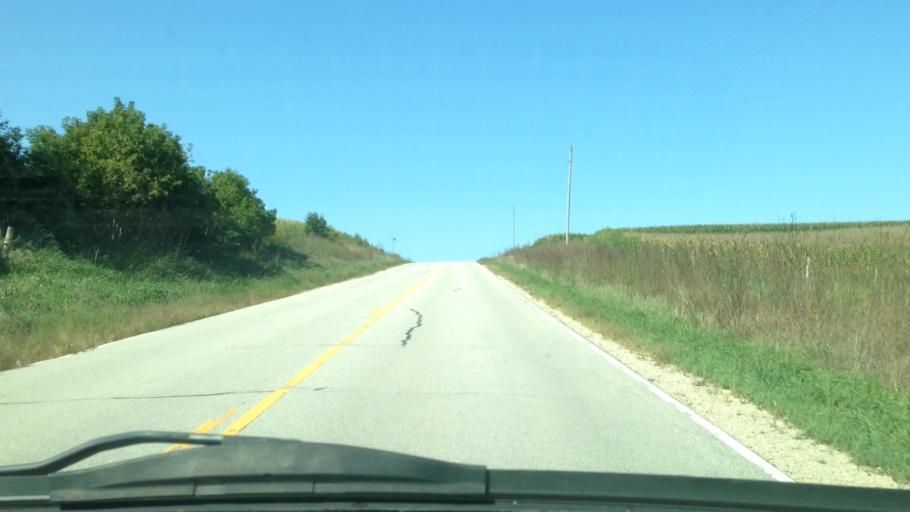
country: US
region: Minnesota
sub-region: Fillmore County
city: Rushford
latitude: 43.6976
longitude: -91.7703
